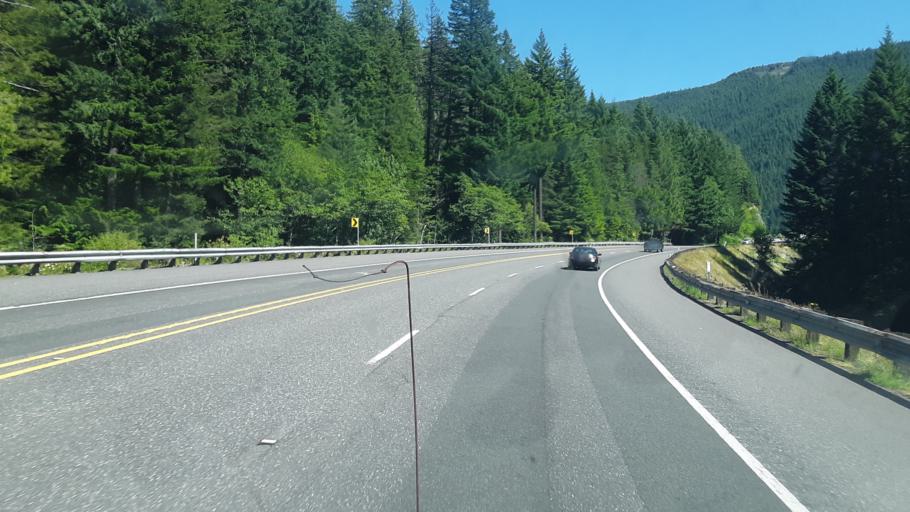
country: US
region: Oregon
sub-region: Clackamas County
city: Mount Hood Village
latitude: 45.3097
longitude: -121.8337
